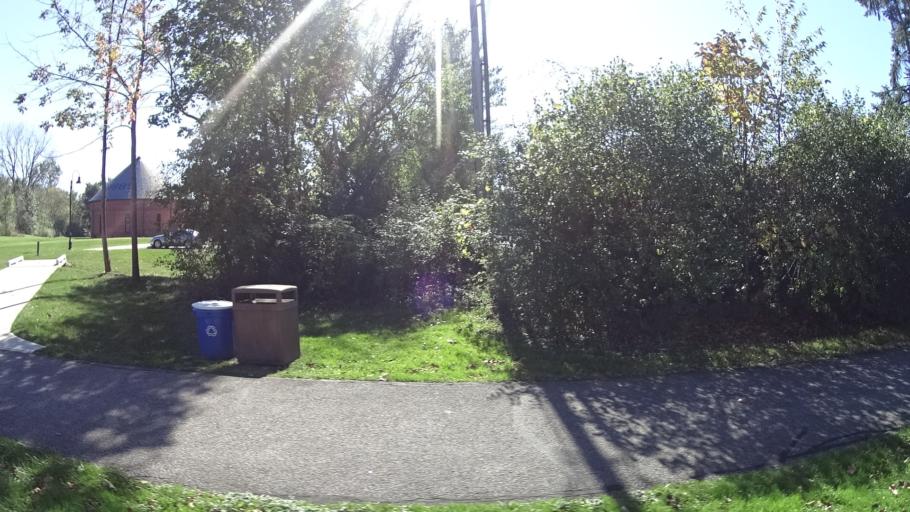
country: US
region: Ohio
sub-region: Lorain County
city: Oberlin
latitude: 41.2849
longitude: -82.2166
